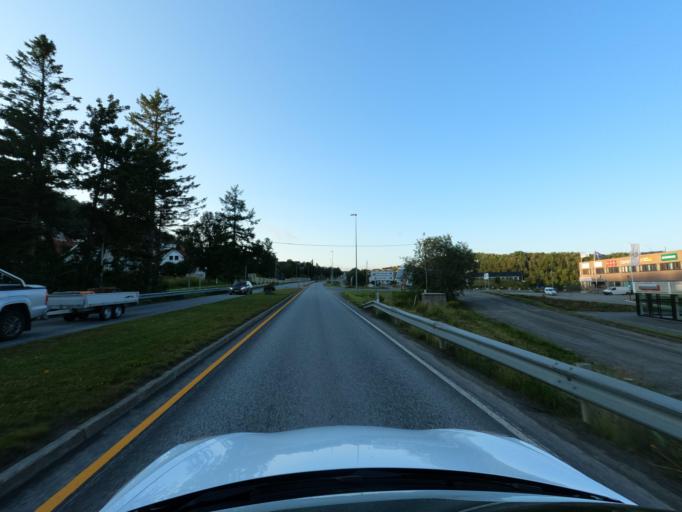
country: NO
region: Troms
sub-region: Harstad
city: Harstad
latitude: 68.7726
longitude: 16.5588
